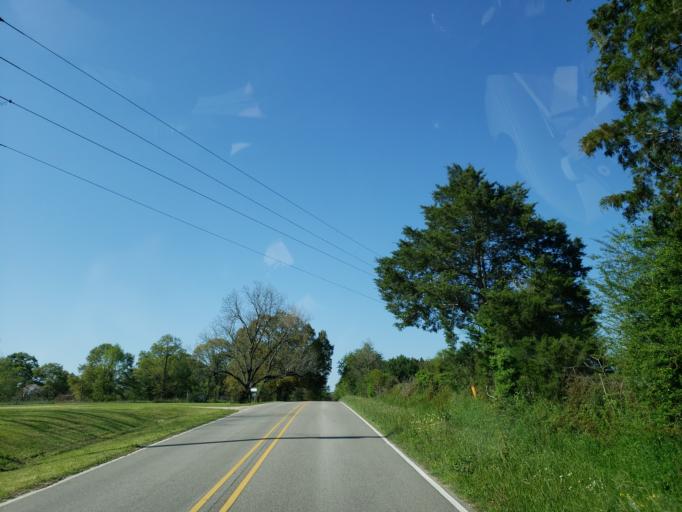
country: US
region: Mississippi
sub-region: Jones County
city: Ellisville
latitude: 31.5857
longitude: -89.3787
